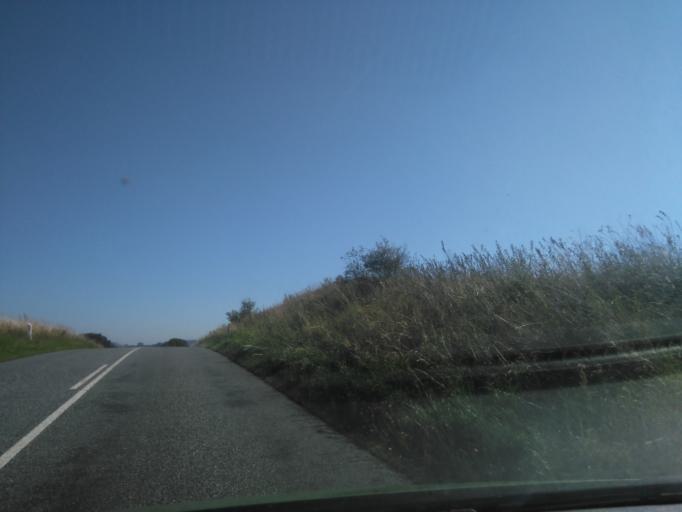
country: DK
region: Central Jutland
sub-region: Syddjurs Kommune
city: Ronde
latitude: 56.1957
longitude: 10.4777
